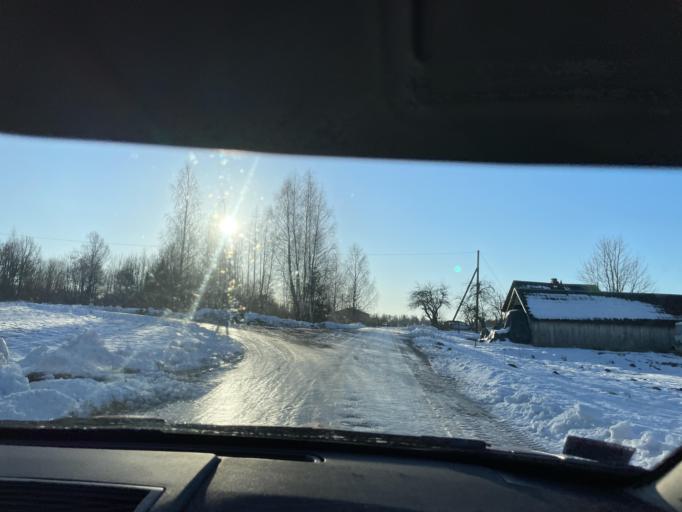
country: LV
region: Ludzas Rajons
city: Ludza
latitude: 56.4672
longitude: 27.6011
